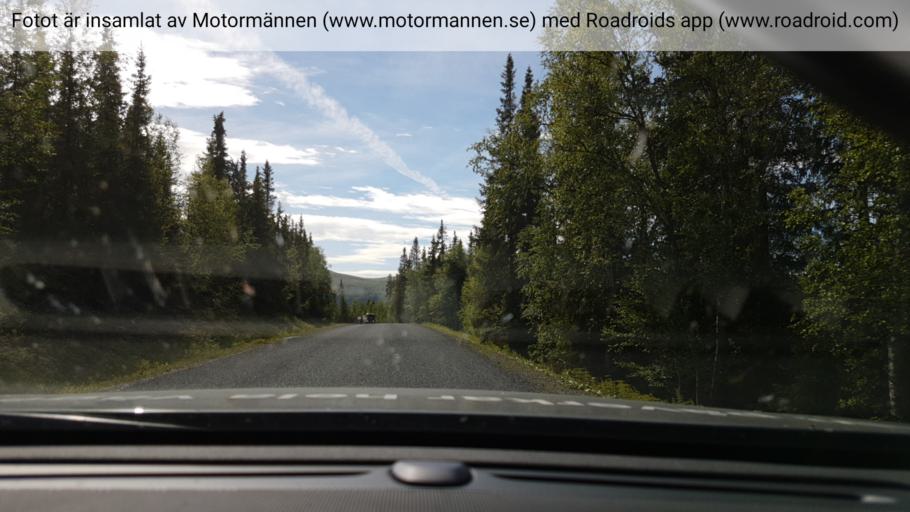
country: SE
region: Vaesterbotten
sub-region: Vilhelmina Kommun
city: Sjoberg
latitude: 65.2724
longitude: 15.3686
